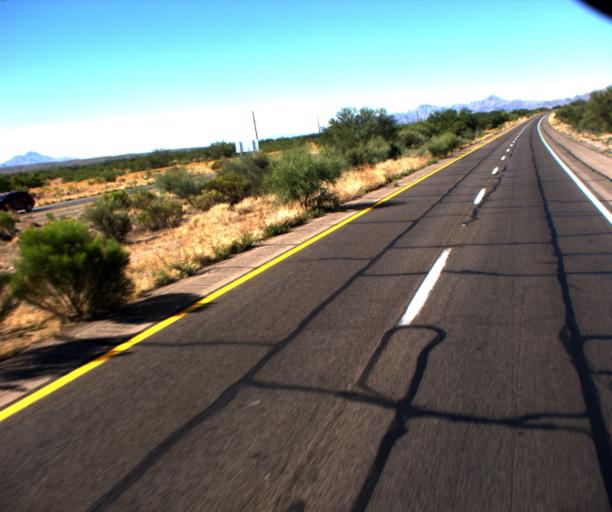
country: US
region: Arizona
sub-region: Pima County
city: Arivaca Junction
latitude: 31.7458
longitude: -111.0465
